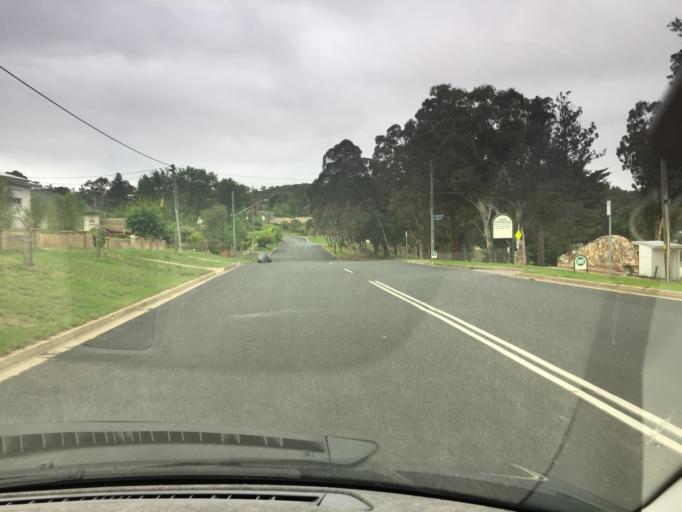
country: AU
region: New South Wales
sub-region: Cooma-Monaro
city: Cooma
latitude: -36.2395
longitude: 149.1242
